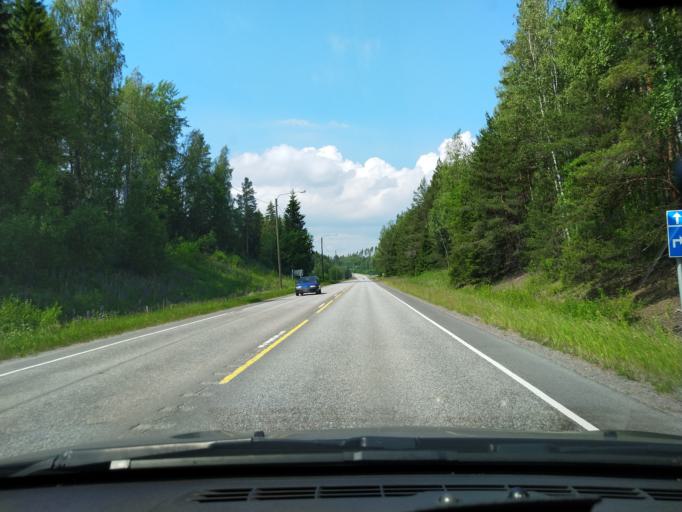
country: FI
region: Uusimaa
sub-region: Helsinki
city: Saukkola
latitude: 60.3809
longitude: 24.0915
